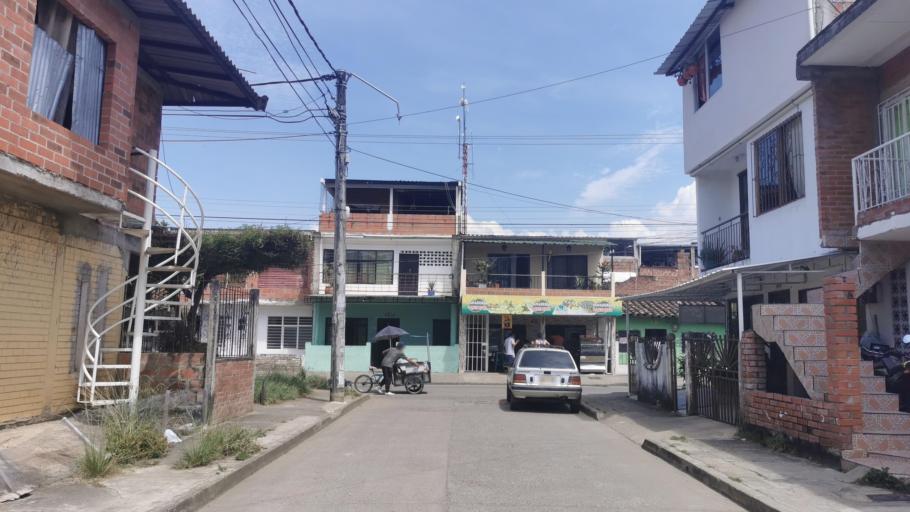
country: CO
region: Valle del Cauca
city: Jamundi
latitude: 3.2543
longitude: -76.5388
